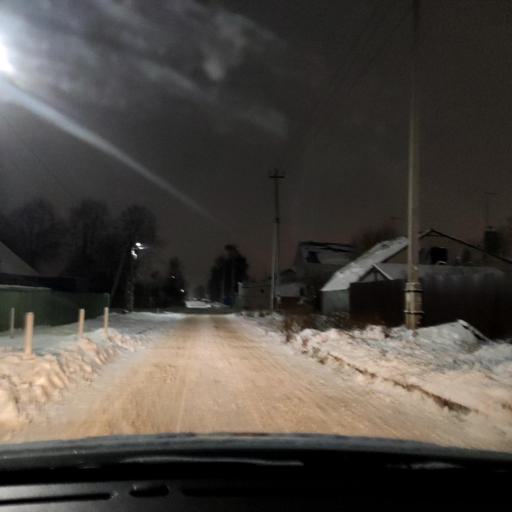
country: RU
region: Tatarstan
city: Staroye Arakchino
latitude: 55.8805
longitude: 49.0469
